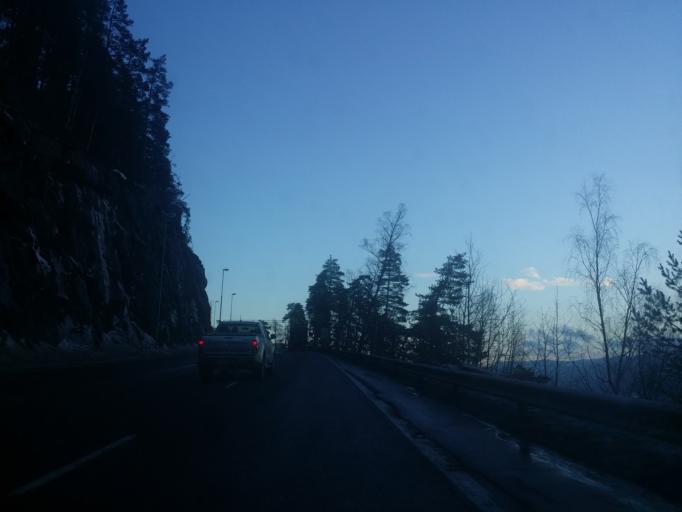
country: NO
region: Buskerud
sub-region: Hole
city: Vik
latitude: 59.9909
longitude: 10.3020
